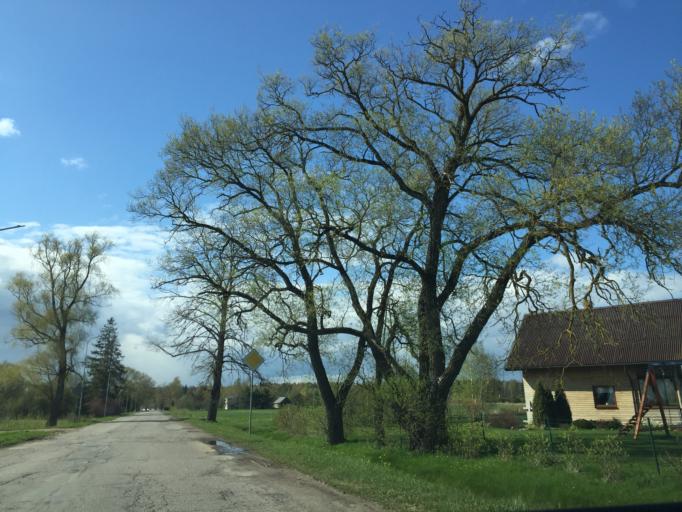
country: LV
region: Jelgava
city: Jelgava
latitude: 56.5625
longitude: 23.7641
